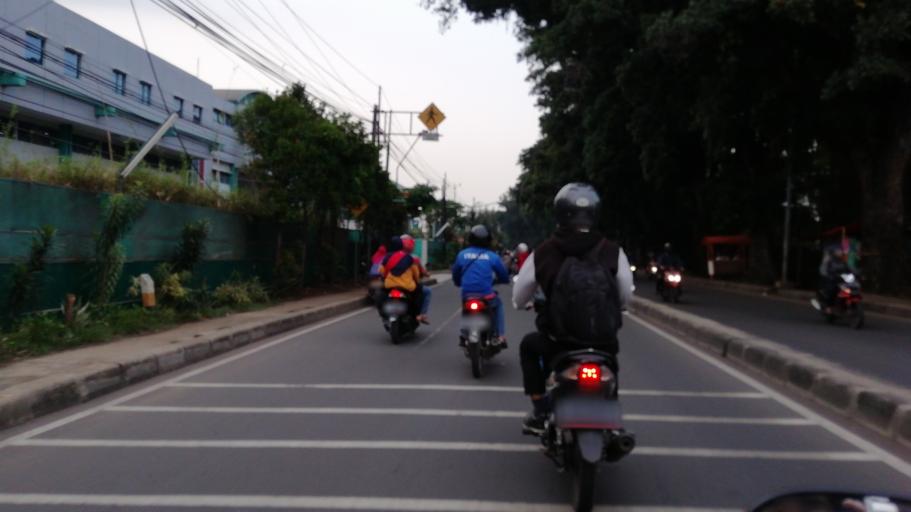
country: ID
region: West Java
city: Cibinong
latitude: -6.4426
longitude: 106.8532
